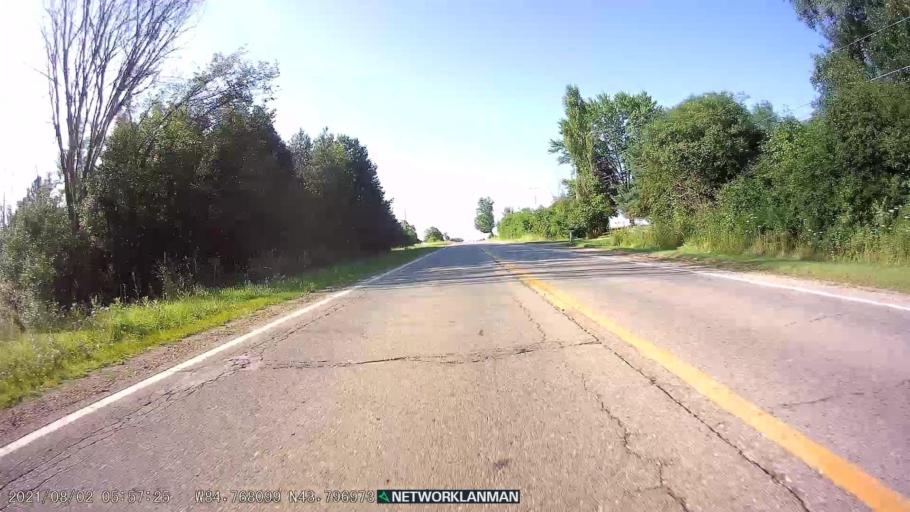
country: US
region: Michigan
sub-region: Clare County
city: Clare
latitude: 43.7976
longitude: -84.7681
